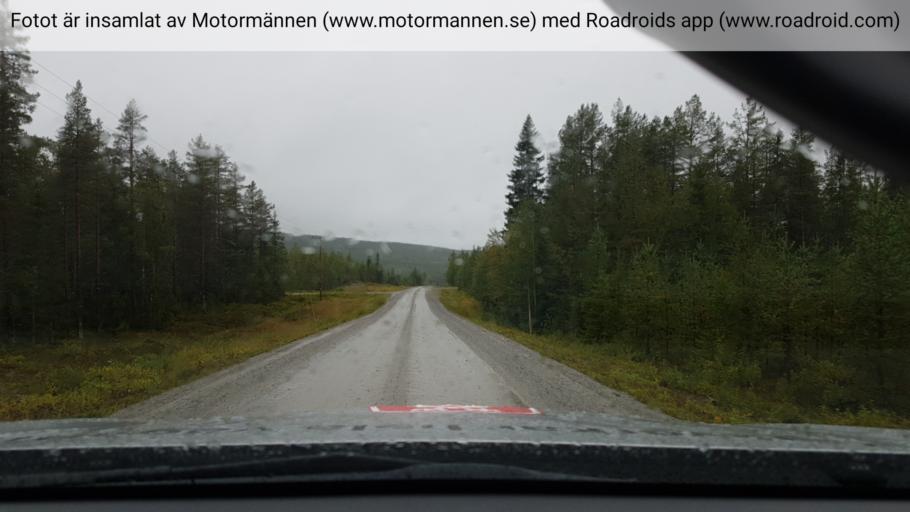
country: SE
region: Vaesterbotten
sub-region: Asele Kommun
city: Insjon
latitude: 64.0851
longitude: 17.8333
